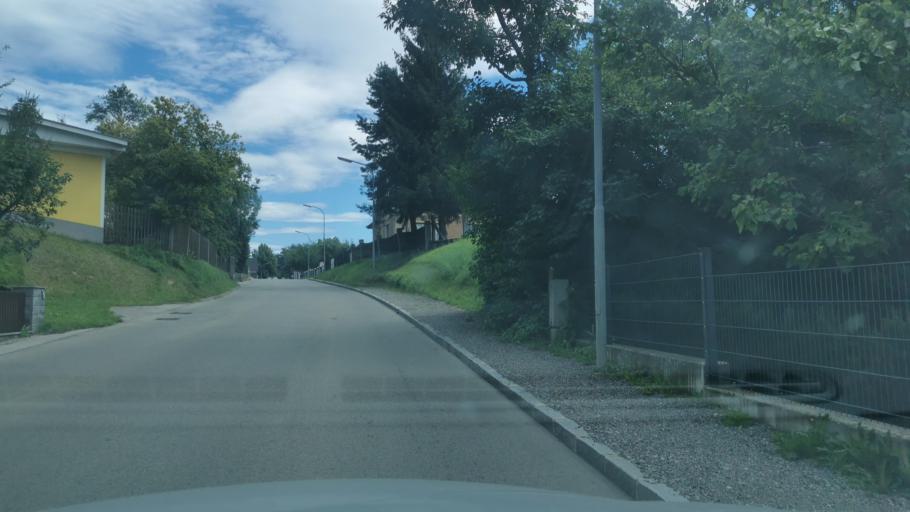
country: AT
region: Lower Austria
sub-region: Politischer Bezirk Sankt Polten
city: Pyhra
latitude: 48.1523
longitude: 15.6404
